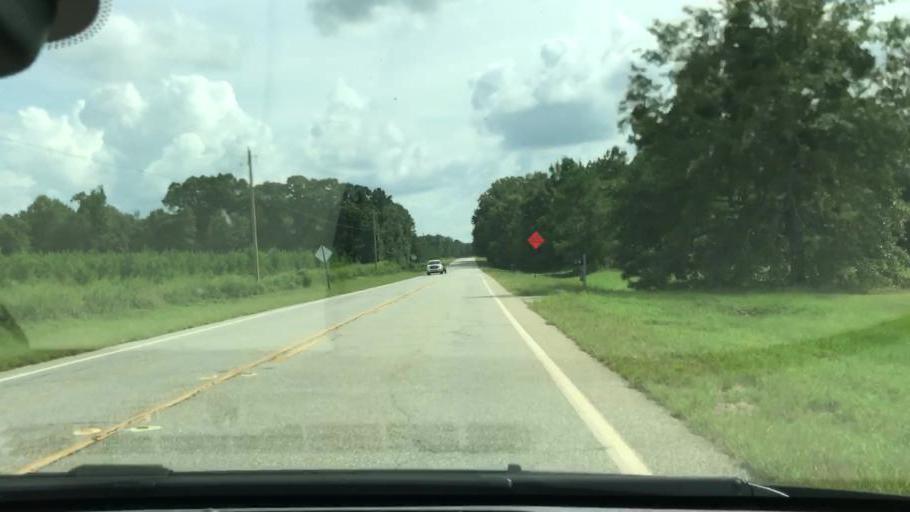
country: US
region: Georgia
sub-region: Clay County
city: Fort Gaines
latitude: 31.7112
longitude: -85.0415
